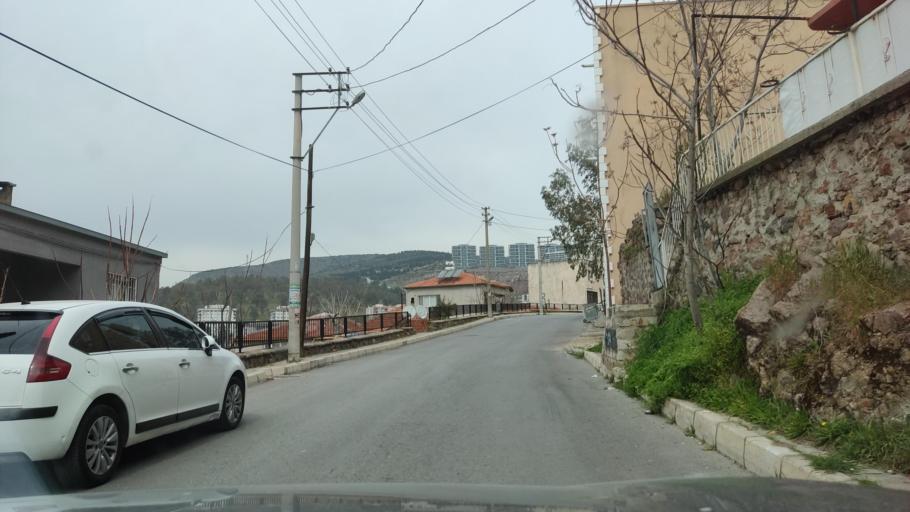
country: TR
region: Izmir
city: Karsiyaka
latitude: 38.4990
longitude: 27.0728
